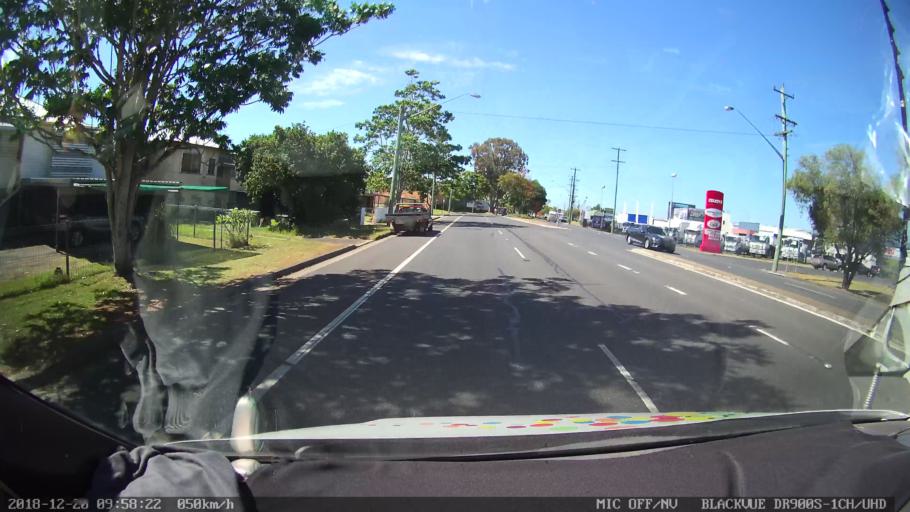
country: AU
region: New South Wales
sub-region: Lismore Municipality
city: Lismore
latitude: -28.8173
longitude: 153.2659
